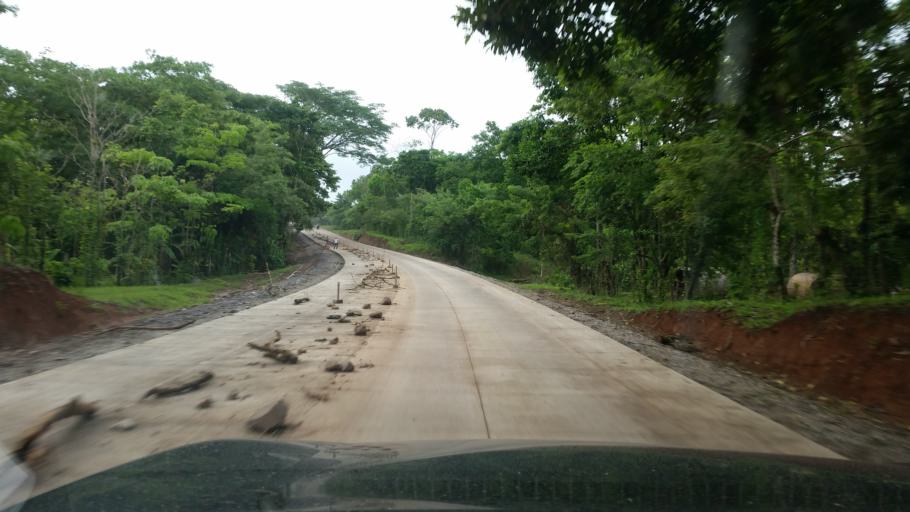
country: NI
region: Matagalpa
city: Rio Blanco
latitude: 13.2025
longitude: -84.9485
